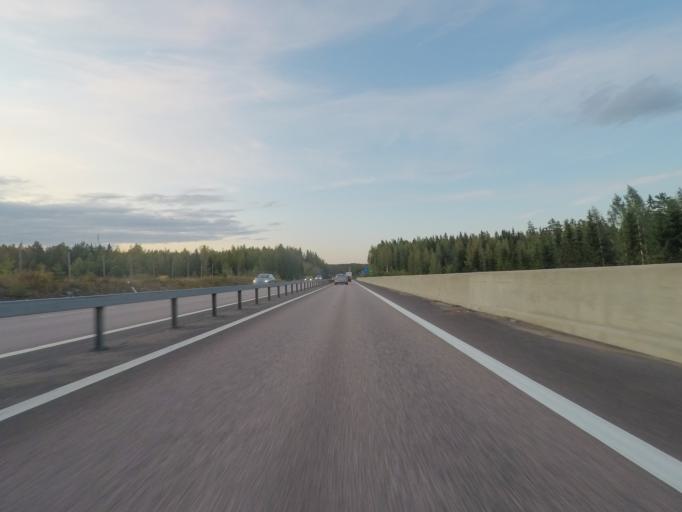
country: FI
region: Central Finland
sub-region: Jyvaeskylae
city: Saeynaetsalo
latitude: 62.2206
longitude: 25.8956
